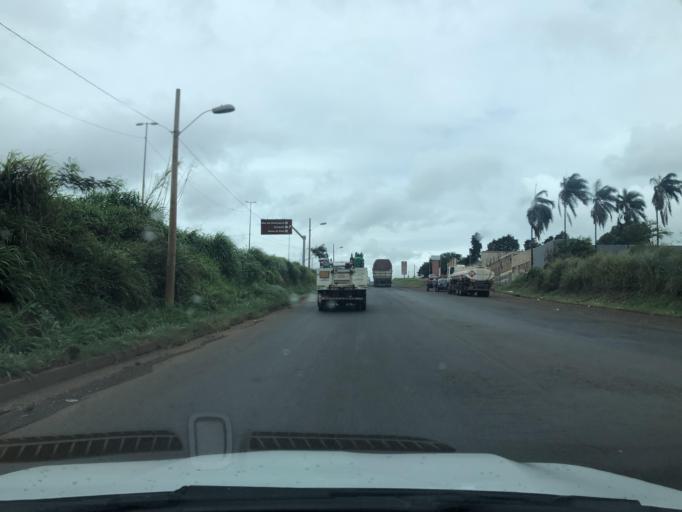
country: BR
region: Minas Gerais
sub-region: Uberaba
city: Uberaba
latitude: -19.7787
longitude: -47.9330
